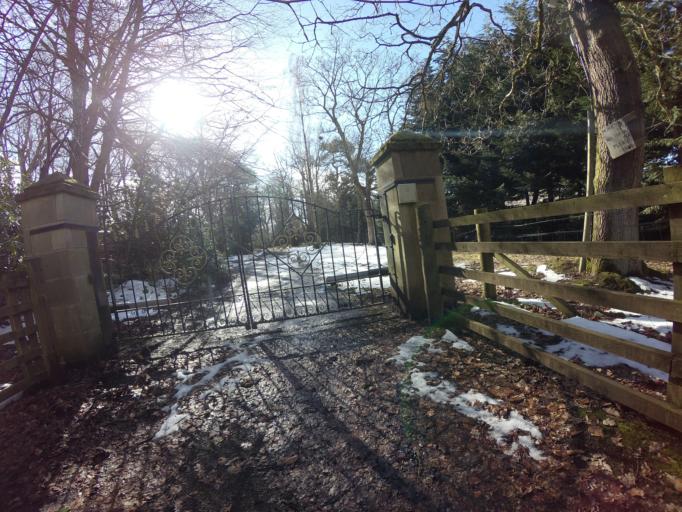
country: GB
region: Scotland
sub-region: West Lothian
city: Mid Calder
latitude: 55.8669
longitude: -3.5066
